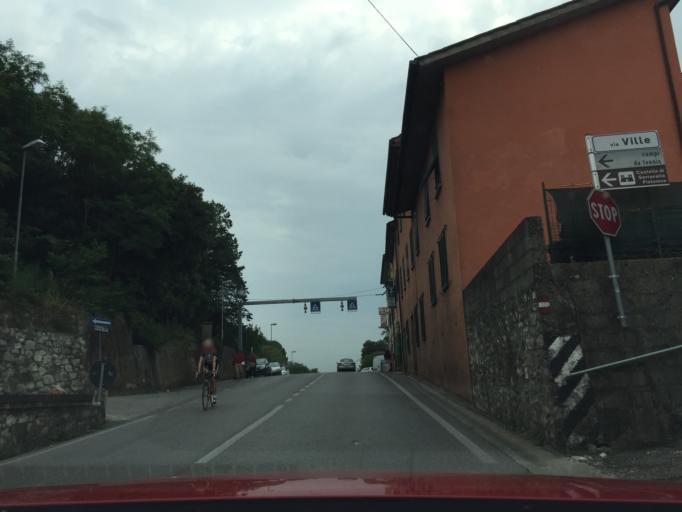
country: IT
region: Tuscany
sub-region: Provincia di Pistoia
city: Serravalle Pistoiese
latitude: 43.9038
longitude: 10.8343
